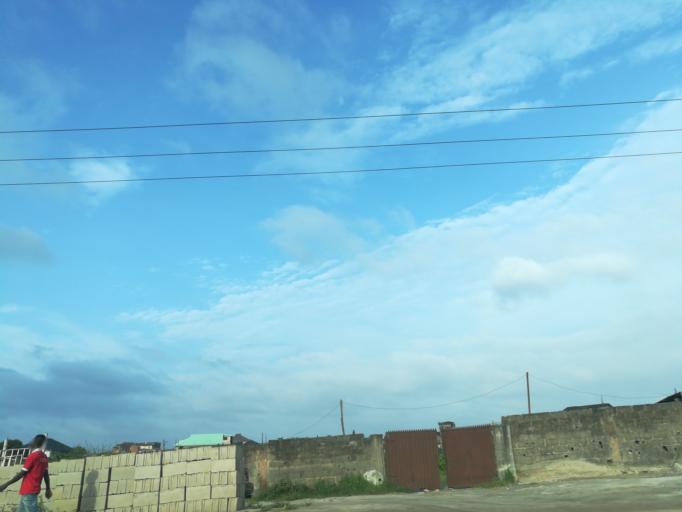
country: NG
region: Lagos
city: Ebute Ikorodu
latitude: 6.6064
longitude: 3.4849
